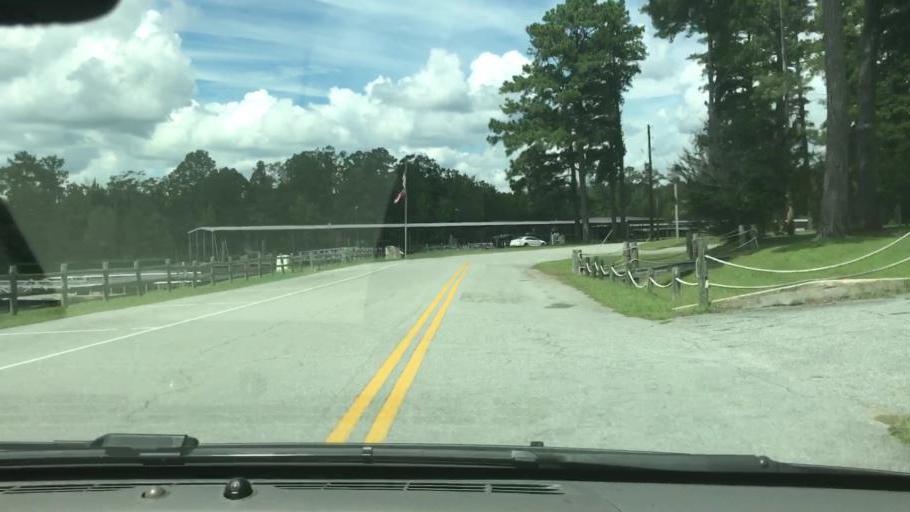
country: US
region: Georgia
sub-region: Quitman County
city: Georgetown
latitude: 32.0894
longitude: -85.0433
